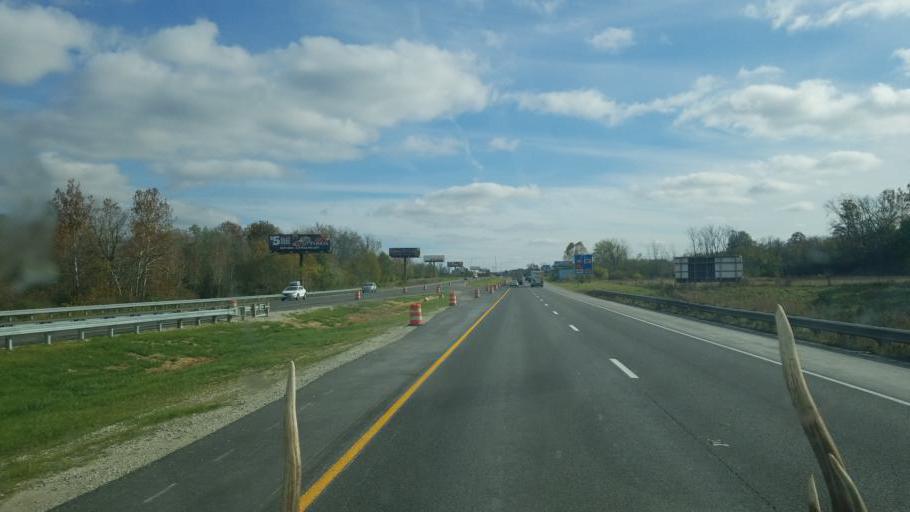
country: US
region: Ohio
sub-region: Preble County
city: New Paris
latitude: 39.8460
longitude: -84.8306
